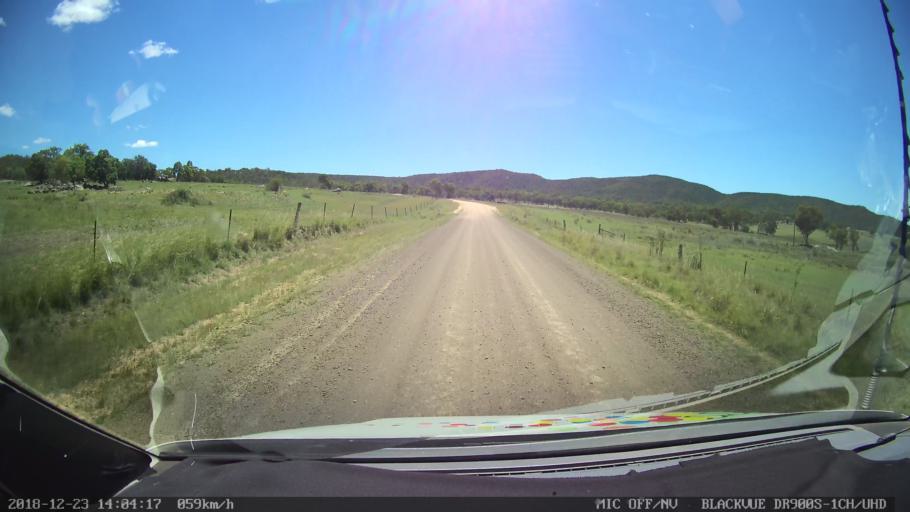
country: AU
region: New South Wales
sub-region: Tamworth Municipality
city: Manilla
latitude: -30.6222
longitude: 151.0919
